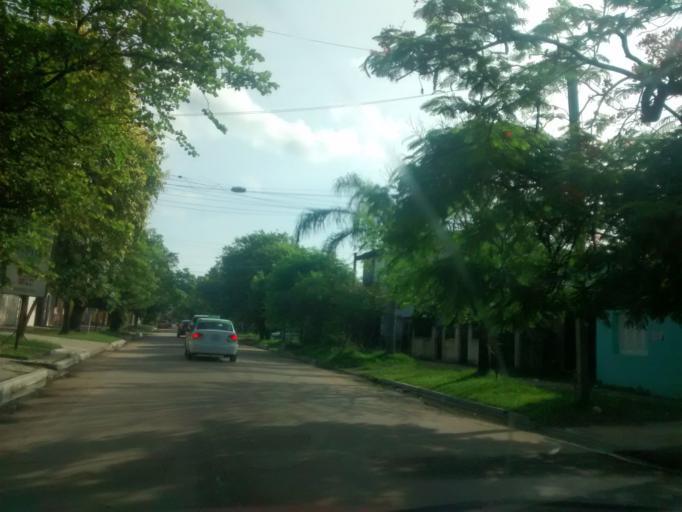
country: AR
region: Chaco
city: Resistencia
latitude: -27.4609
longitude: -58.9870
